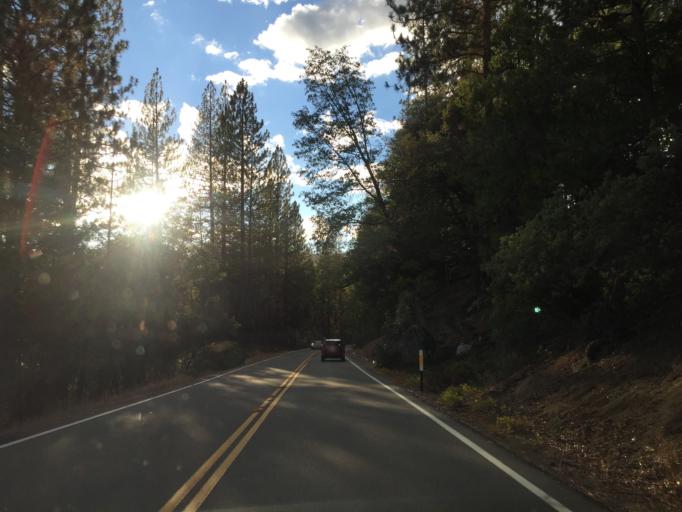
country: US
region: California
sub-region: Madera County
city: Ahwahnee
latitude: 37.5324
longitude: -119.6405
